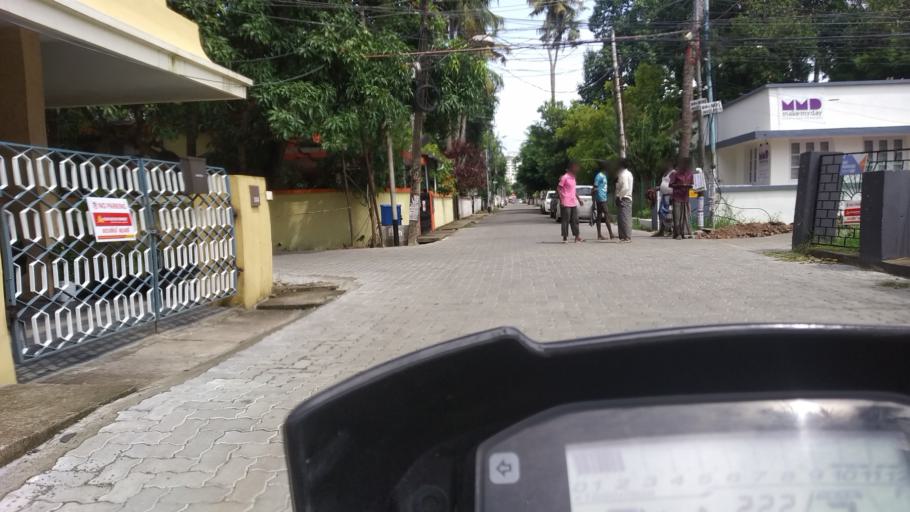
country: IN
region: Kerala
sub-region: Ernakulam
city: Cochin
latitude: 9.9626
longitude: 76.2984
